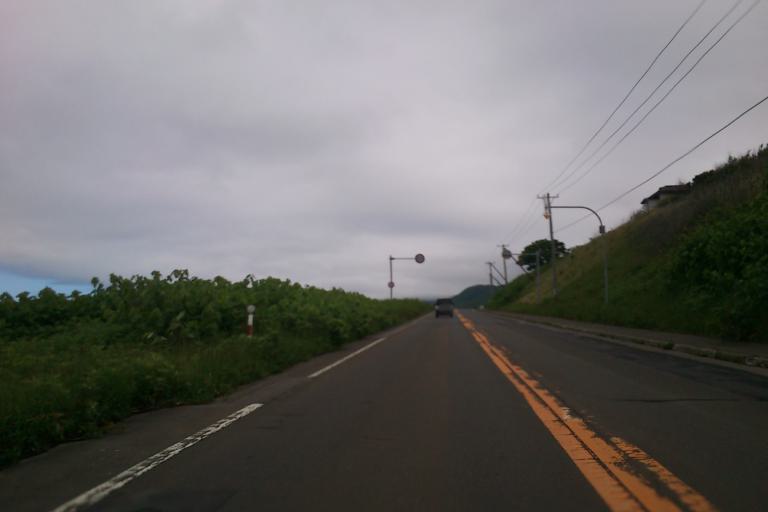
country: JP
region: Hokkaido
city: Ishikari
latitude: 43.4041
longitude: 141.4308
